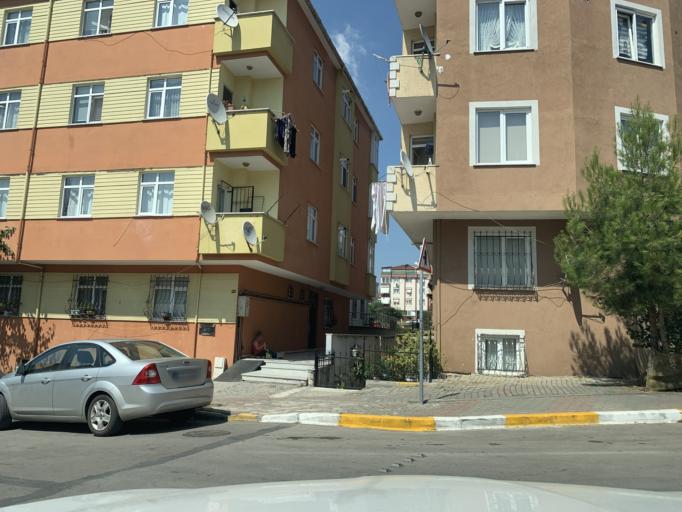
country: TR
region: Istanbul
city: Pendik
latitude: 40.8608
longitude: 29.2783
